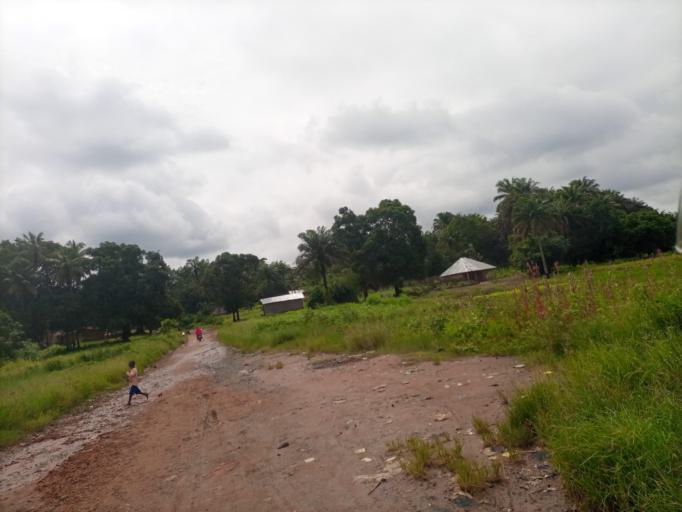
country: SL
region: Northern Province
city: Sawkta
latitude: 8.6350
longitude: -13.1993
